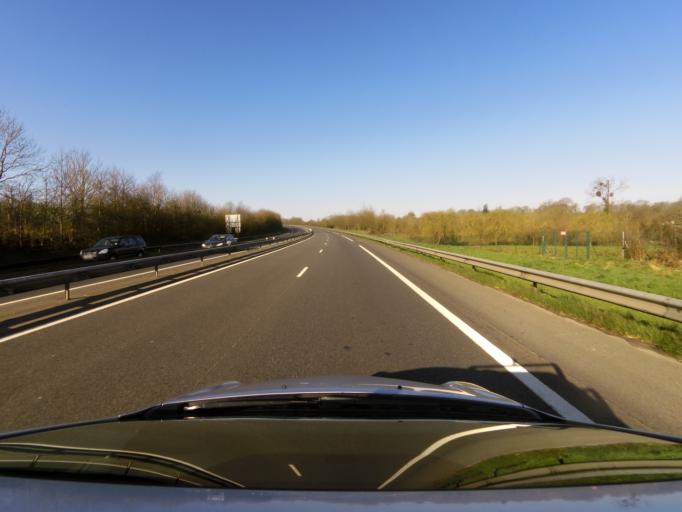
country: FR
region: Lower Normandy
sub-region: Departement du Calvados
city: Saint-Martin-des-Besaces
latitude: 49.0097
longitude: -0.8942
